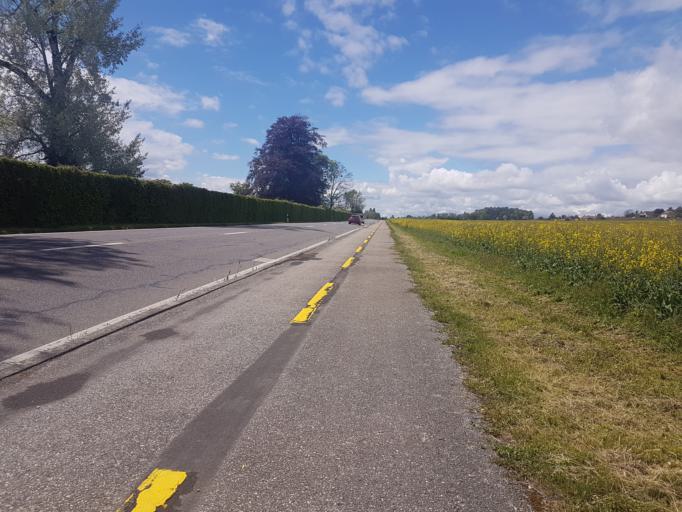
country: CH
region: Vaud
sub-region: Nyon District
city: Rolle
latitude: 46.4387
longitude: 6.3123
